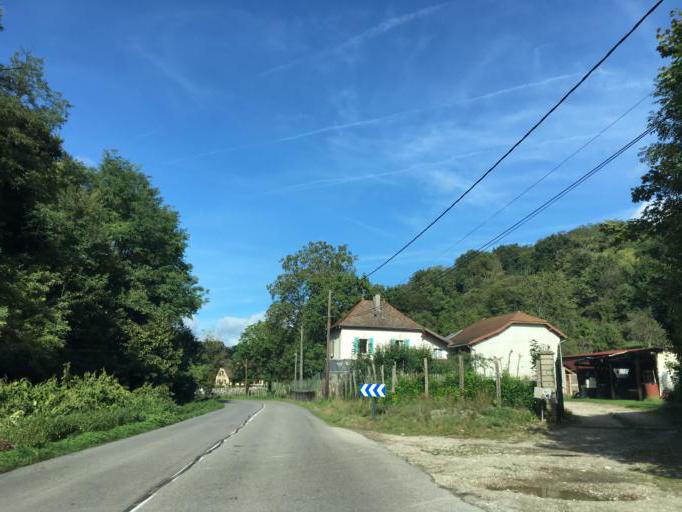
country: FR
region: Rhone-Alpes
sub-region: Departement de l'Isere
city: Saint-Clair-de-la-Tour
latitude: 45.5679
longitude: 5.4781
